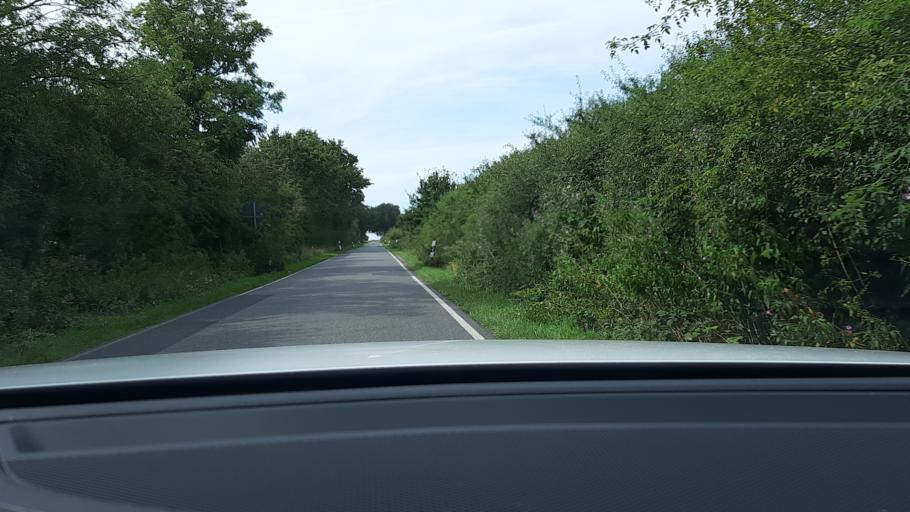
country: DE
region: Schleswig-Holstein
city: Heidekamp
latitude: 53.8681
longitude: 10.4938
